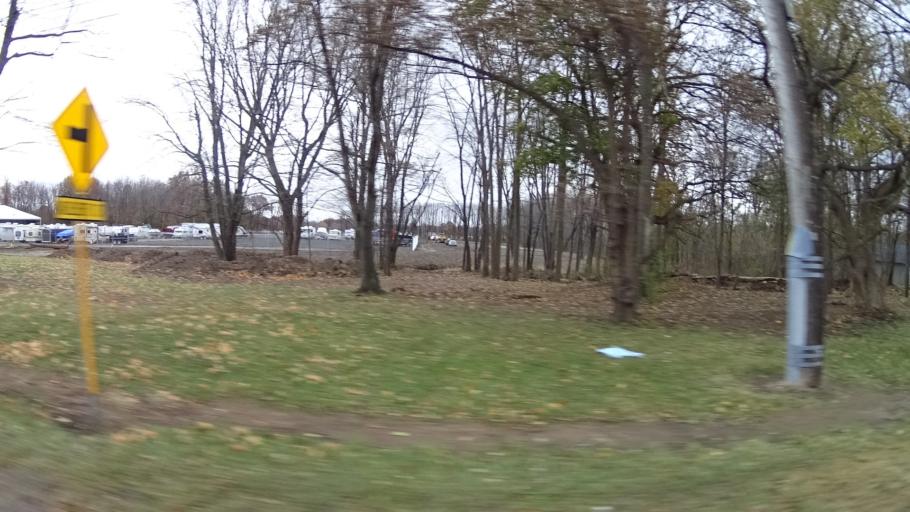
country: US
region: Ohio
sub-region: Lorain County
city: Elyria
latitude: 41.3926
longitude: -82.1304
